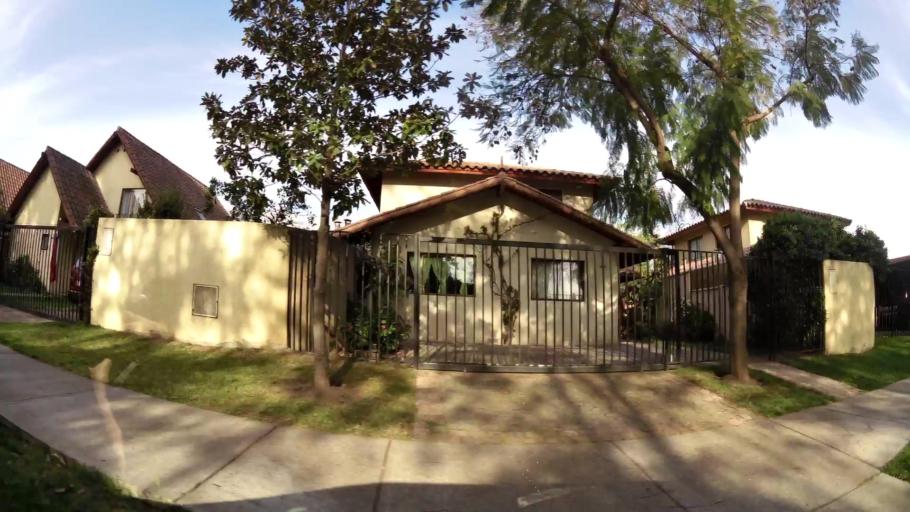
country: CL
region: Santiago Metropolitan
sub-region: Provincia de Santiago
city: Villa Presidente Frei, Nunoa, Santiago, Chile
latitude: -33.5049
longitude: -70.5533
